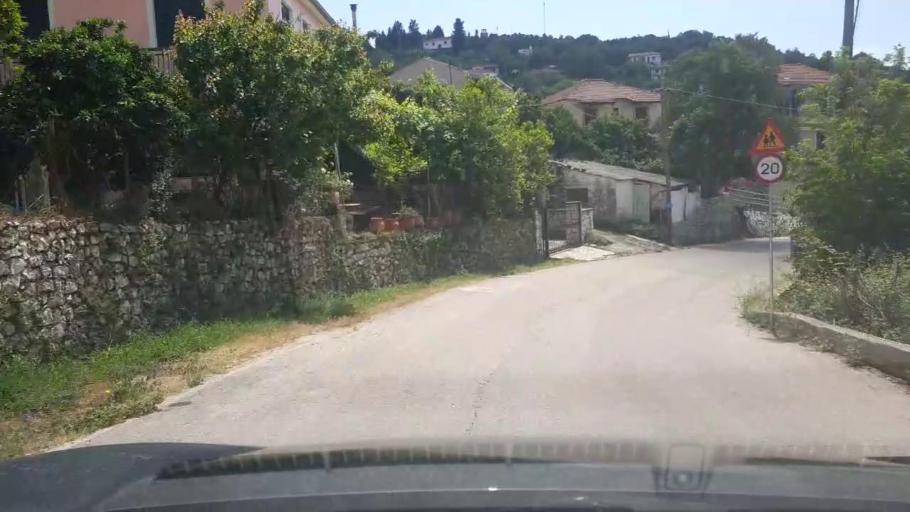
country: GR
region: Ionian Islands
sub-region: Lefkada
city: Nidri
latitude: 38.6431
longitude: 20.7069
